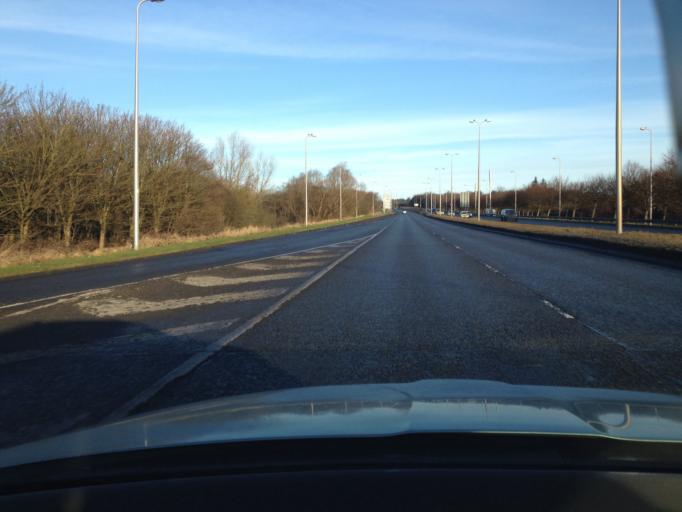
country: GB
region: Scotland
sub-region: West Lothian
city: Livingston
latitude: 55.8913
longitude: -3.5034
